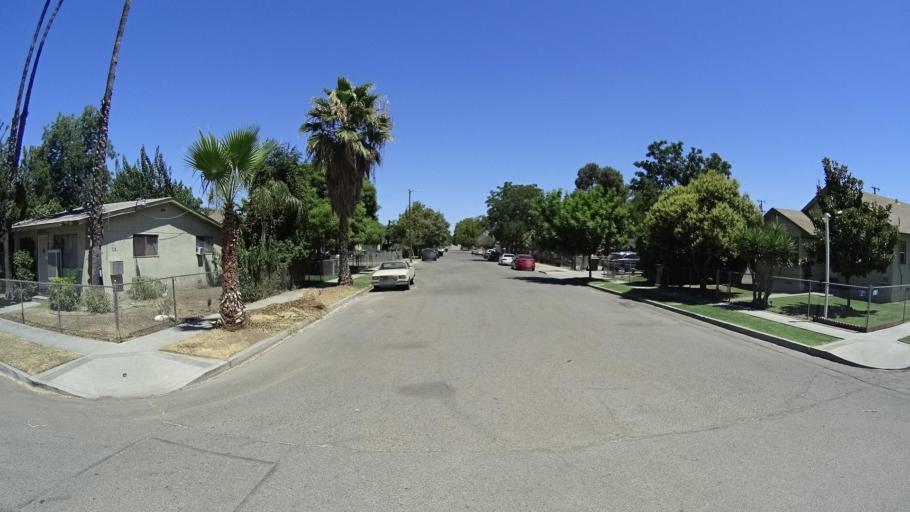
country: US
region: California
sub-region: Fresno County
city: Fresno
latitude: 36.7033
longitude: -119.7560
